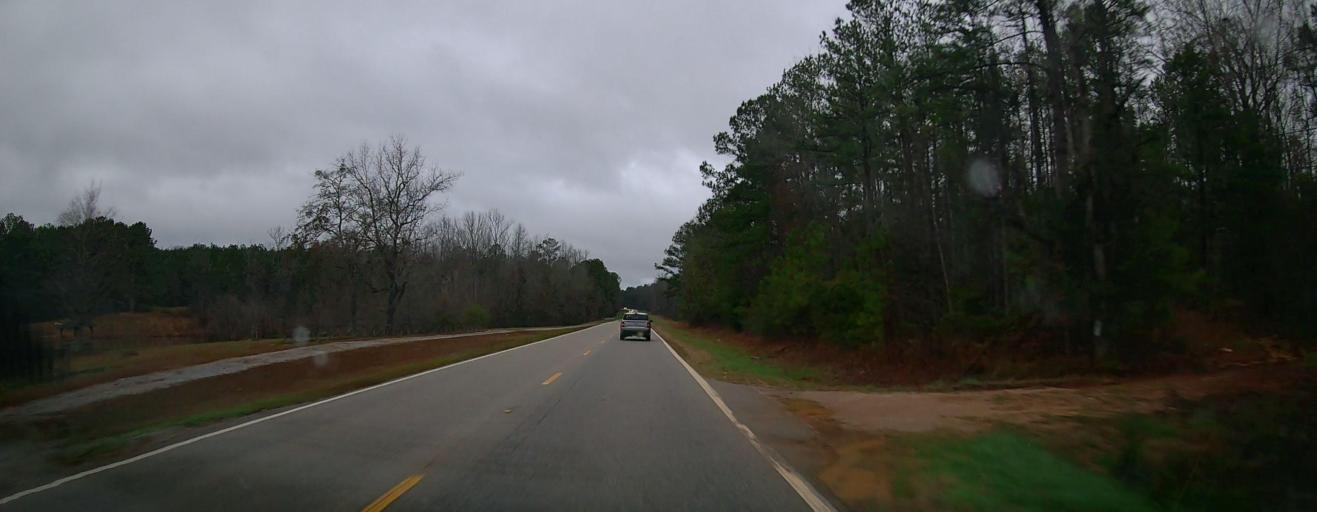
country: US
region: Alabama
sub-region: Bibb County
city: Centreville
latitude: 32.8892
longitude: -86.9847
